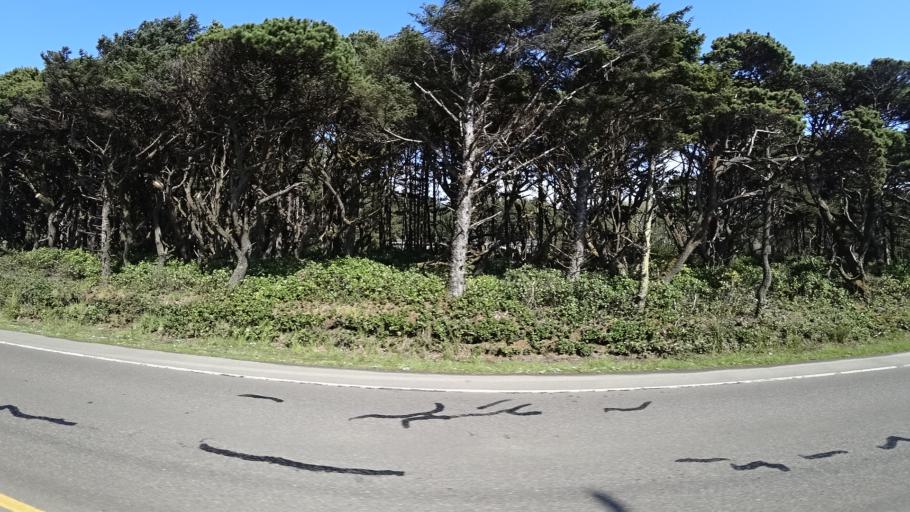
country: US
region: Oregon
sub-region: Lincoln County
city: Newport
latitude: 44.5541
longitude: -124.0718
